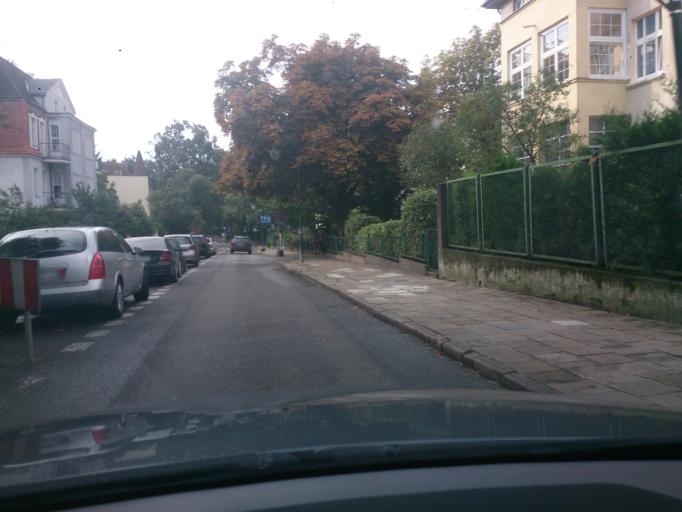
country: PL
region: Pomeranian Voivodeship
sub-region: Sopot
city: Sopot
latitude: 54.4386
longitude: 18.5572
